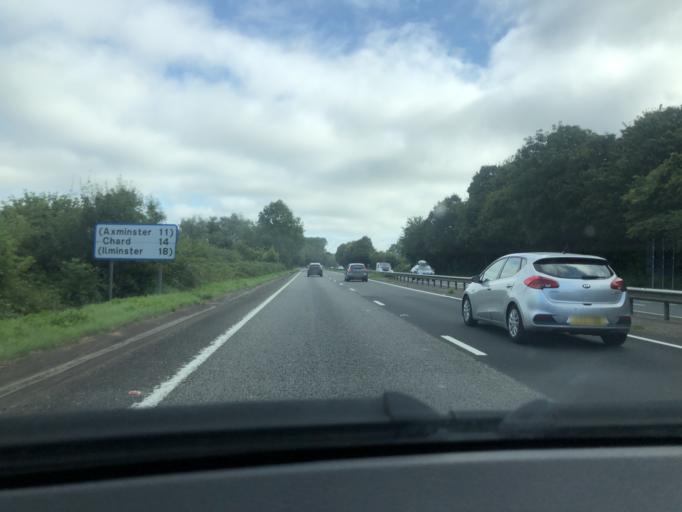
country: GB
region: England
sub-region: Devon
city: Honiton
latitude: 50.7978
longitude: -3.2061
